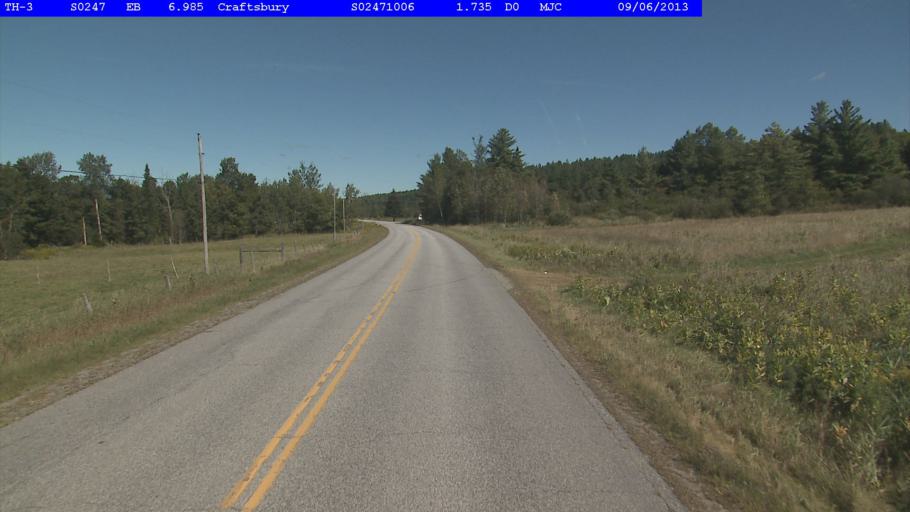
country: US
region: Vermont
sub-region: Caledonia County
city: Hardwick
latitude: 44.6364
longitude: -72.4200
